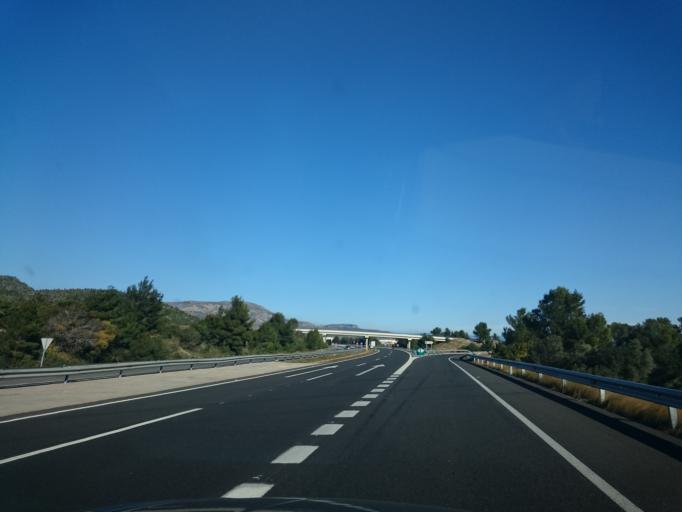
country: ES
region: Catalonia
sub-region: Provincia de Tarragona
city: Colldejou
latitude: 40.9993
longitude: 0.9090
